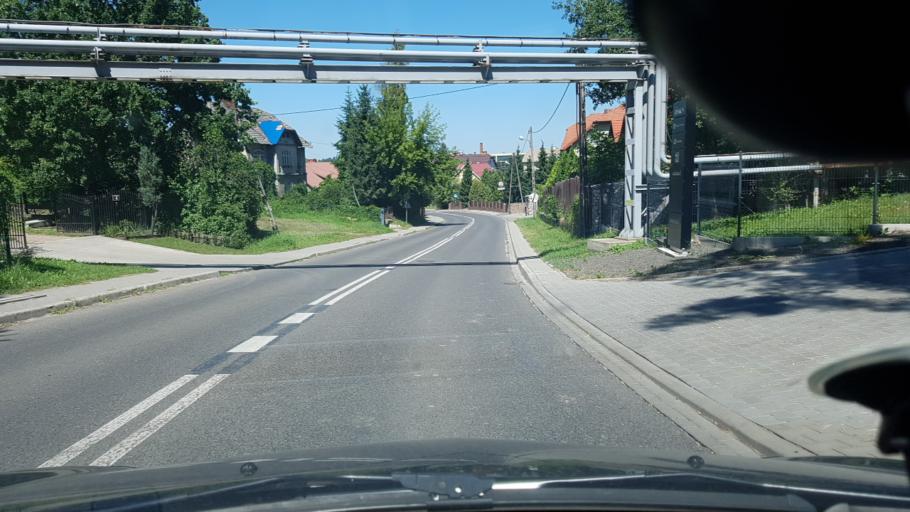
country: PL
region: Lesser Poland Voivodeship
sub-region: Powiat wielicki
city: Wieliczka
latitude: 49.9825
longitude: 20.0471
